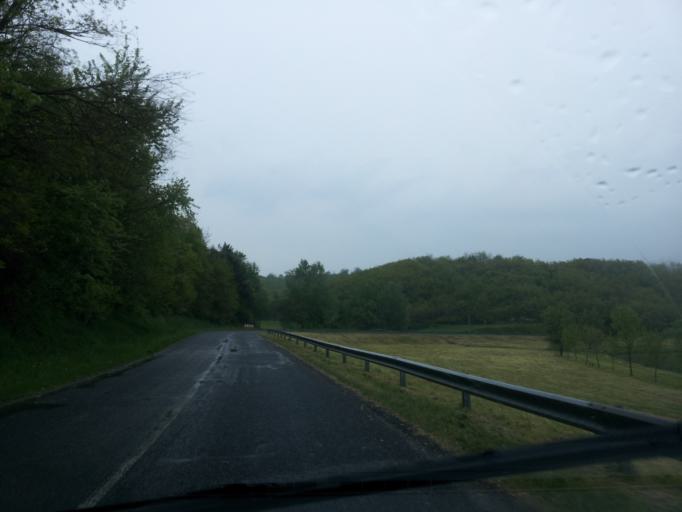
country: HU
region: Tolna
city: Szentgalpuszta
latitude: 46.2717
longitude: 18.6297
